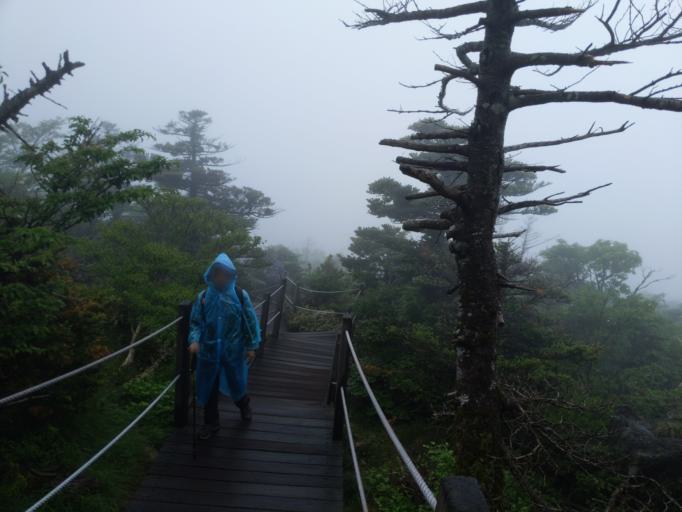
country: KR
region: Jeju-do
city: Seogwipo
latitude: 33.3628
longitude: 126.5404
